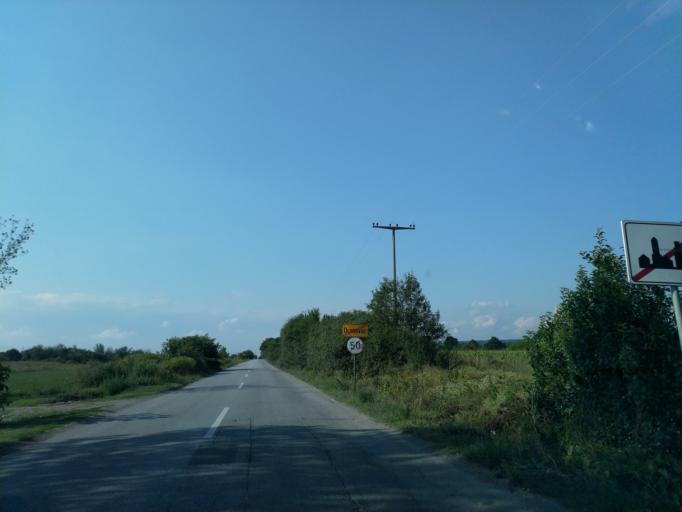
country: RS
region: Central Serbia
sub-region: Rasinski Okrug
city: Cicevac
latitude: 43.7708
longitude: 21.4272
